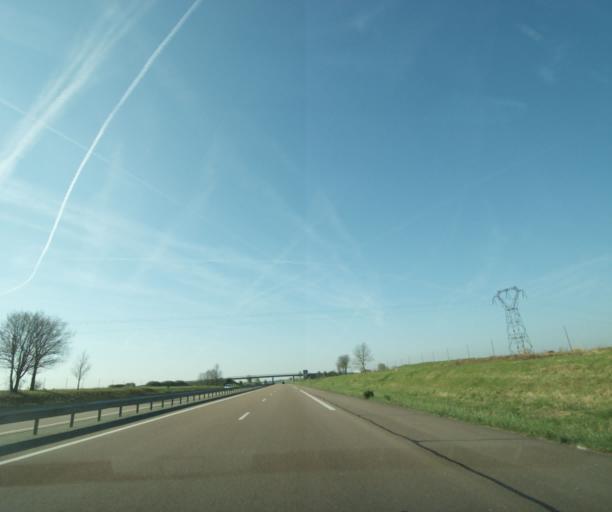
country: FR
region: Ile-de-France
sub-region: Departement de Seine-et-Marne
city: Souppes-sur-Loing
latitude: 48.2001
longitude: 2.7706
